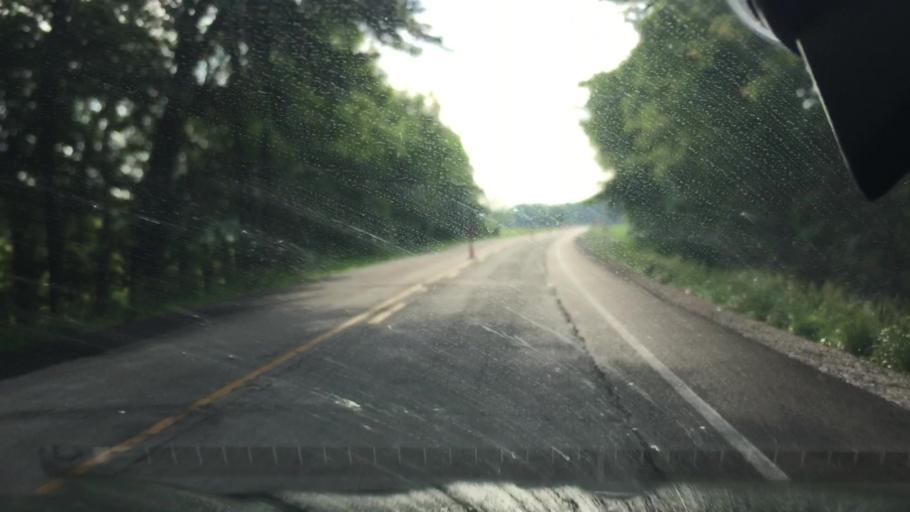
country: US
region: Kentucky
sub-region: Hancock County
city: Lewisport
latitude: 37.9506
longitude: -86.9596
